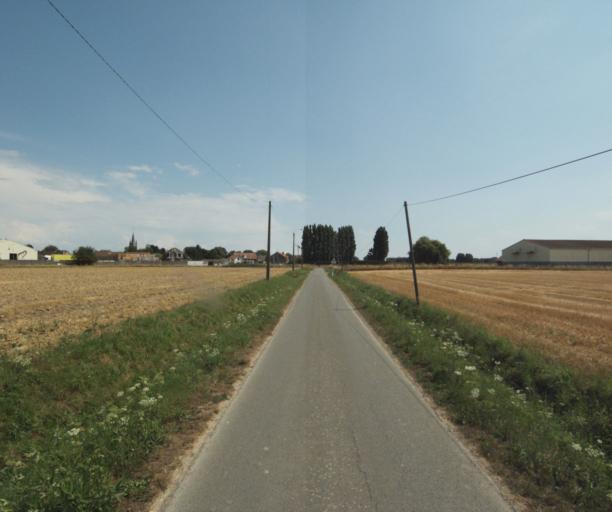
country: FR
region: Nord-Pas-de-Calais
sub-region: Departement du Nord
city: Comines
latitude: 50.7411
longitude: 3.0071
